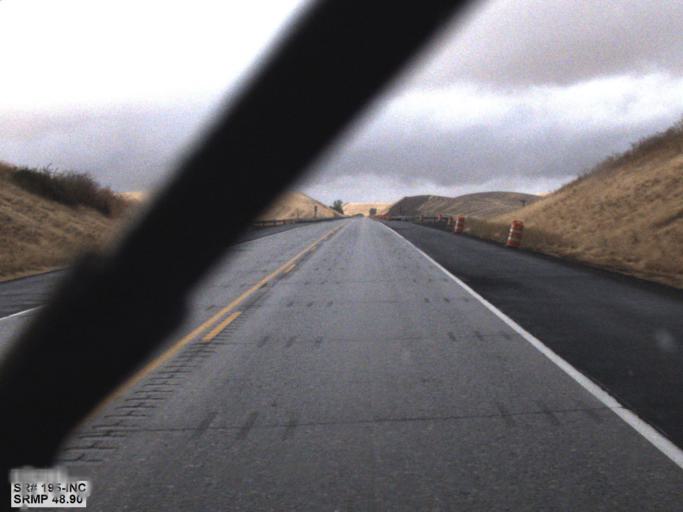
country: US
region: Washington
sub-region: Whitman County
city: Colfax
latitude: 47.0189
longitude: -117.3570
